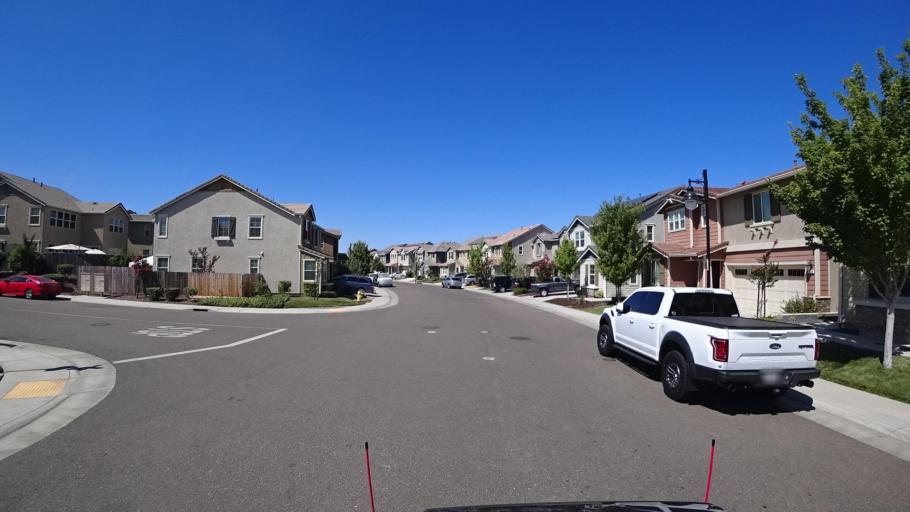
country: US
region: California
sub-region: Placer County
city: Rocklin
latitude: 38.8255
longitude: -121.2903
